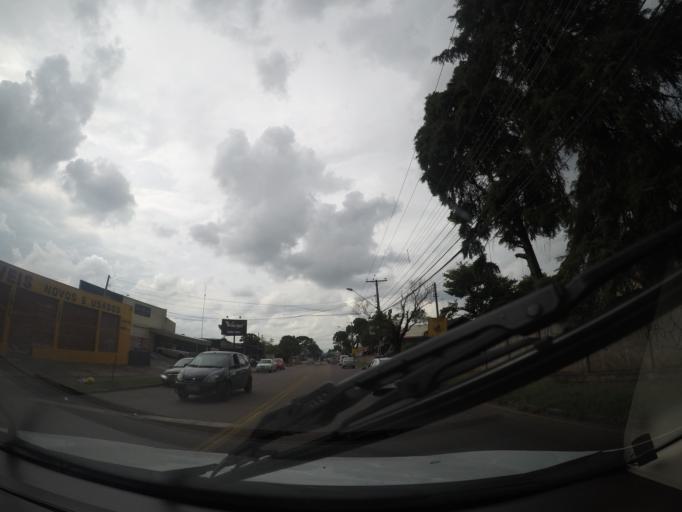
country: BR
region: Parana
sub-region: Sao Jose Dos Pinhais
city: Sao Jose dos Pinhais
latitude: -25.5216
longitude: -49.2388
